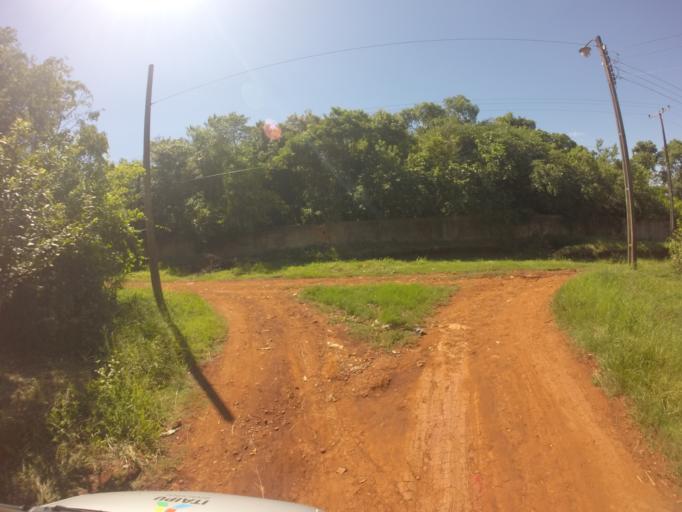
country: PY
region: Alto Parana
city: Ciudad del Este
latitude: -25.4394
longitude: -54.6385
